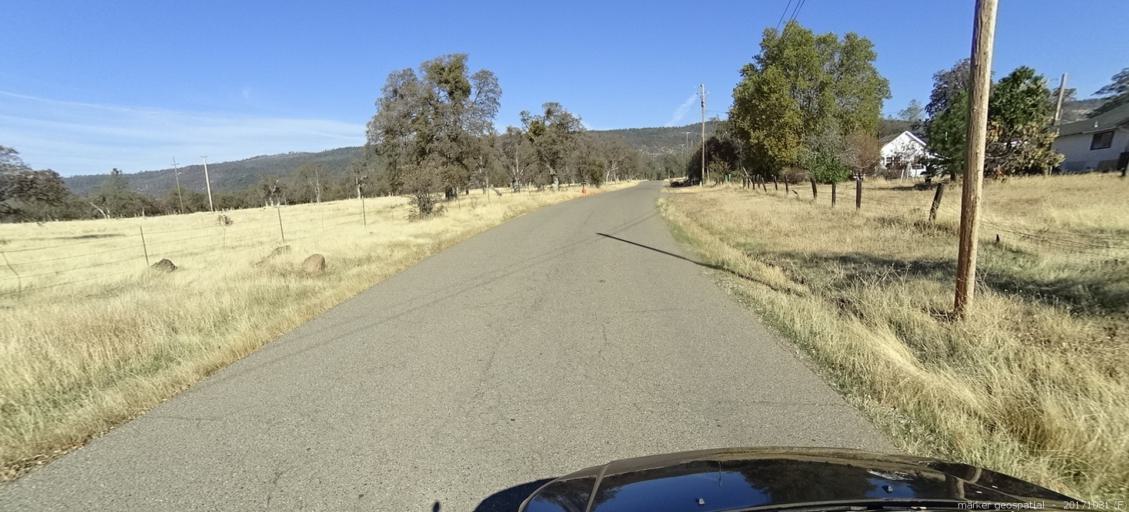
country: US
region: California
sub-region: Shasta County
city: Shingletown
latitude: 40.4392
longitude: -121.8712
